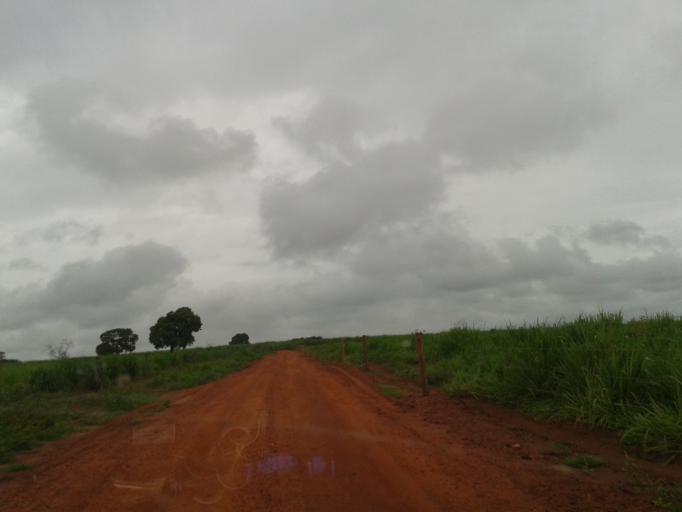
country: BR
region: Minas Gerais
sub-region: Santa Vitoria
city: Santa Vitoria
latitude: -18.7289
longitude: -49.9705
